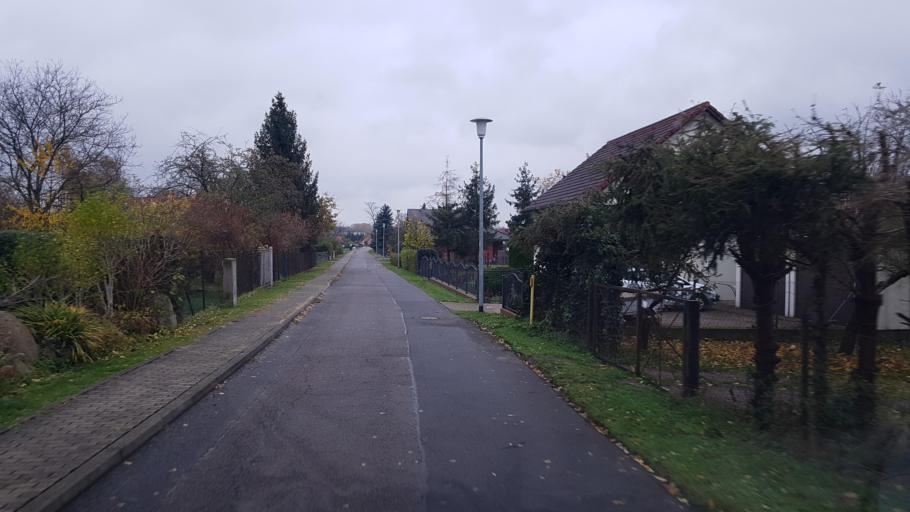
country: DE
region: Brandenburg
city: Drebkau
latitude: 51.6970
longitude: 14.2483
